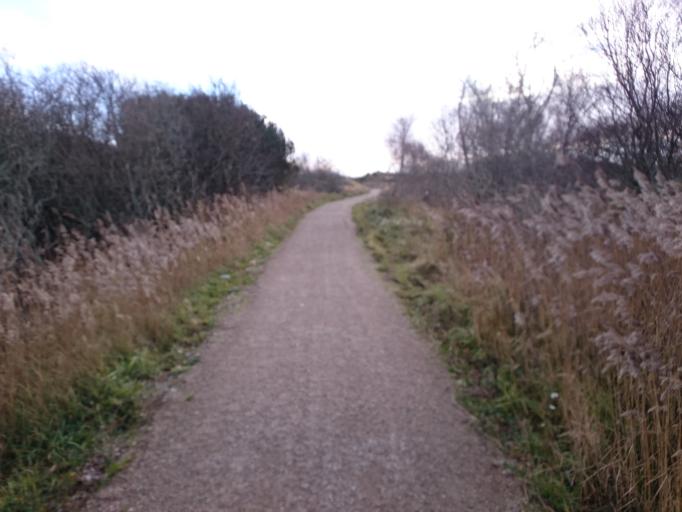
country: DK
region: North Denmark
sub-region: Frederikshavn Kommune
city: Skagen
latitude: 57.7395
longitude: 10.6266
